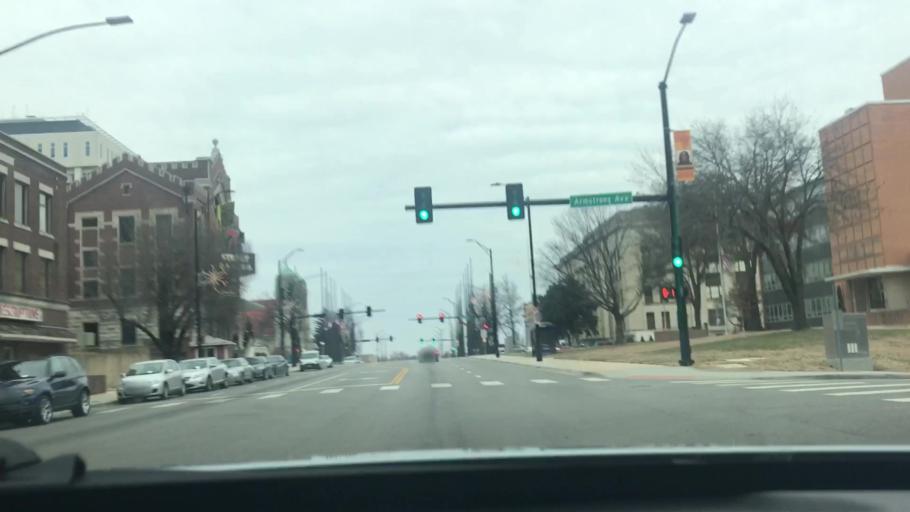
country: US
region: Kansas
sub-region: Wyandotte County
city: Kansas City
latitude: 39.1147
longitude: -94.6269
